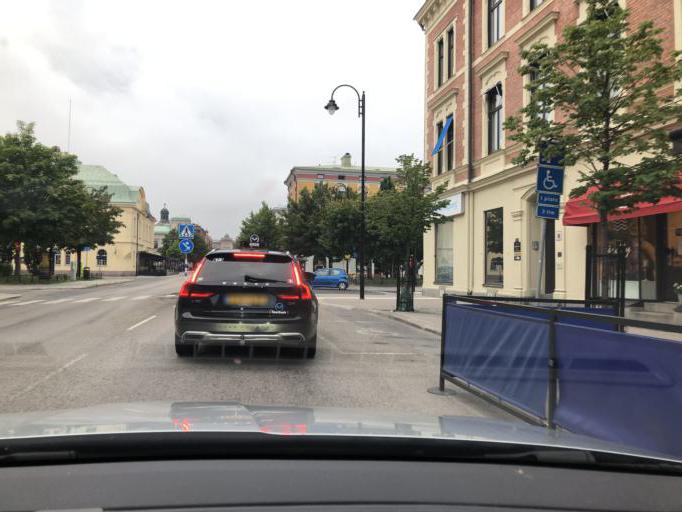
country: SE
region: Vaesternorrland
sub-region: Sundsvalls Kommun
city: Sundsvall
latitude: 62.3888
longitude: 17.3083
